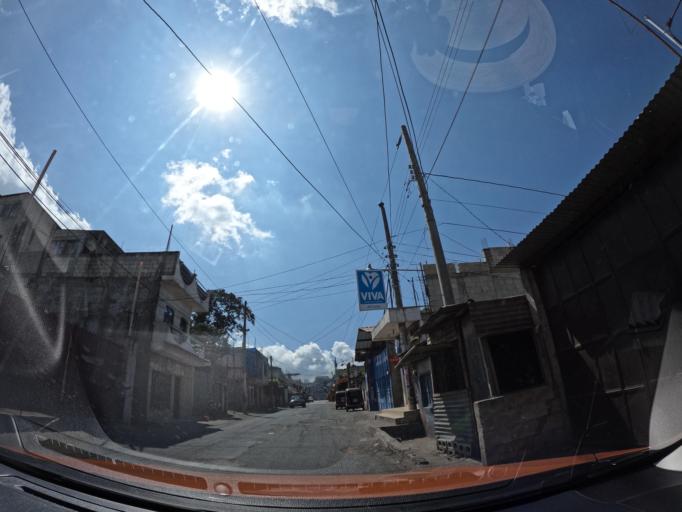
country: GT
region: Solola
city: Santiago Atitlan
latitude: 14.6454
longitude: -91.2264
